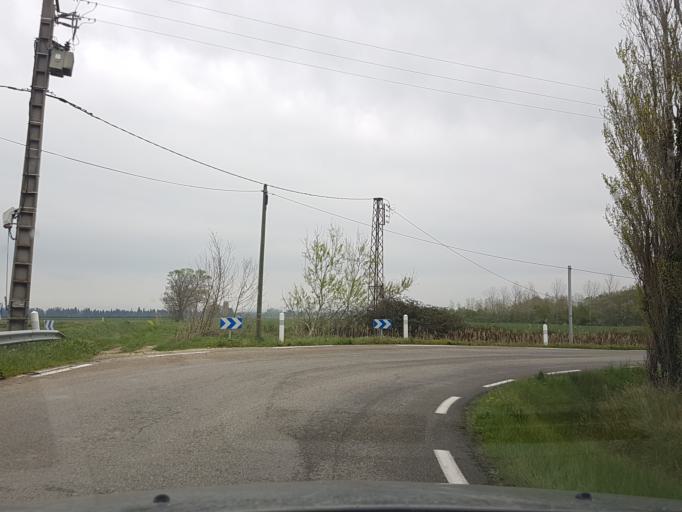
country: FR
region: Provence-Alpes-Cote d'Azur
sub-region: Departement du Vaucluse
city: Bedarrides
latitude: 44.0334
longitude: 4.9197
